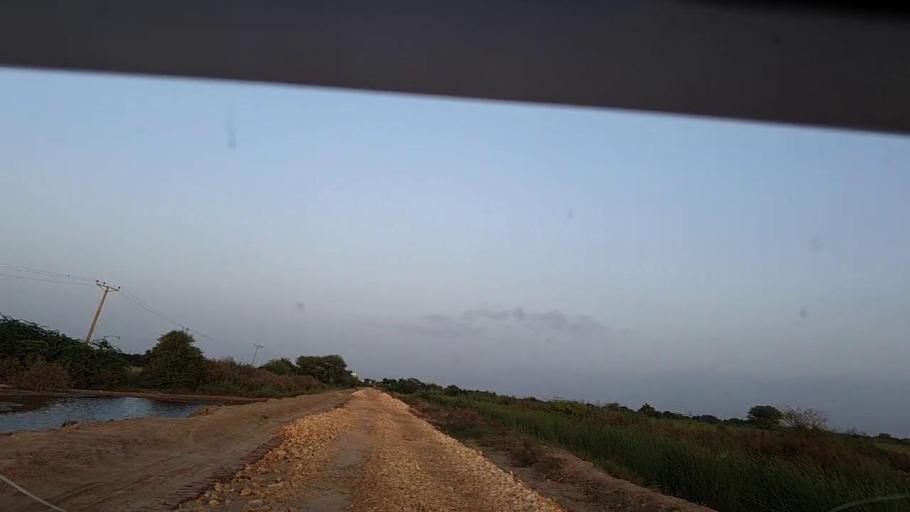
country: PK
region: Sindh
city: Kadhan
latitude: 24.5293
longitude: 68.9520
